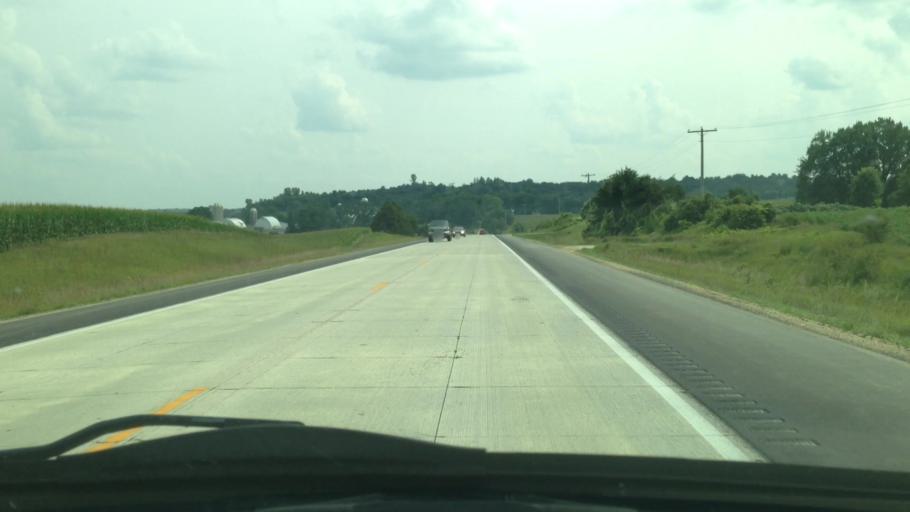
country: US
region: Minnesota
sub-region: Olmsted County
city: Oronoco
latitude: 44.1535
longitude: -92.4194
